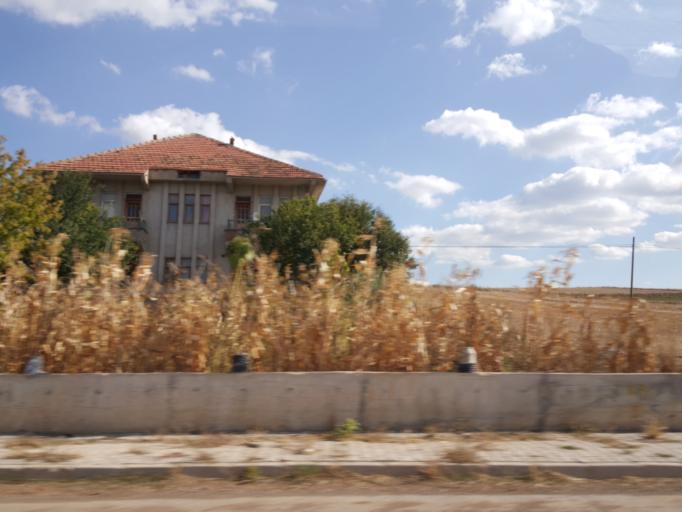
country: TR
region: Tokat
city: Sulusaray
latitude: 39.9844
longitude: 36.0698
